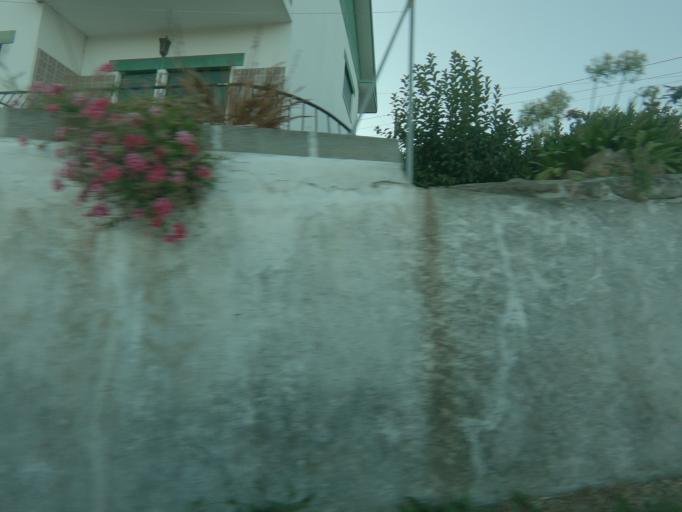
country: PT
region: Vila Real
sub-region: Mesao Frio
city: Mesao Frio
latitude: 41.1818
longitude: -7.8526
